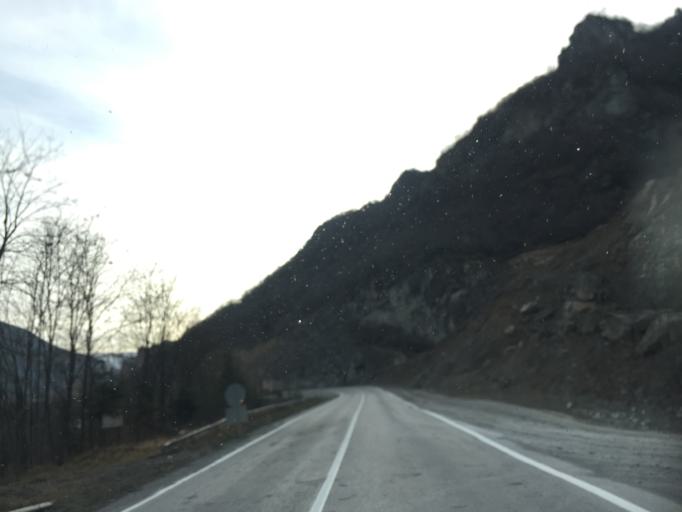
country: TR
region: Trabzon
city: Macka
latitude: 40.7239
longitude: 39.5211
